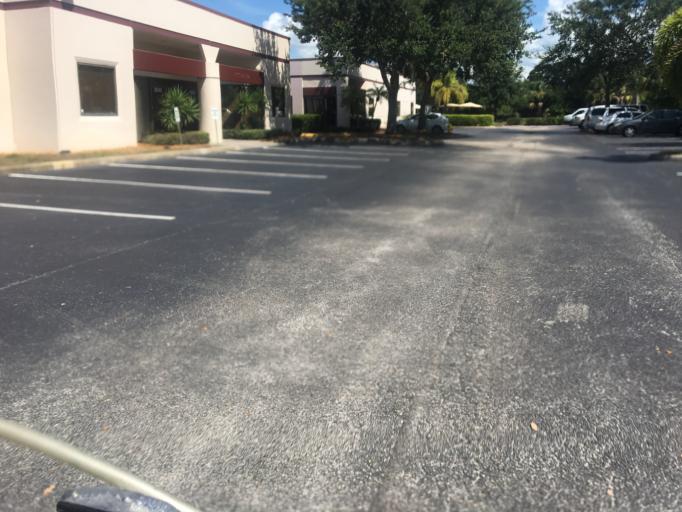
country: US
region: Florida
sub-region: Martin County
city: Palm City
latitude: 27.1679
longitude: -80.3012
